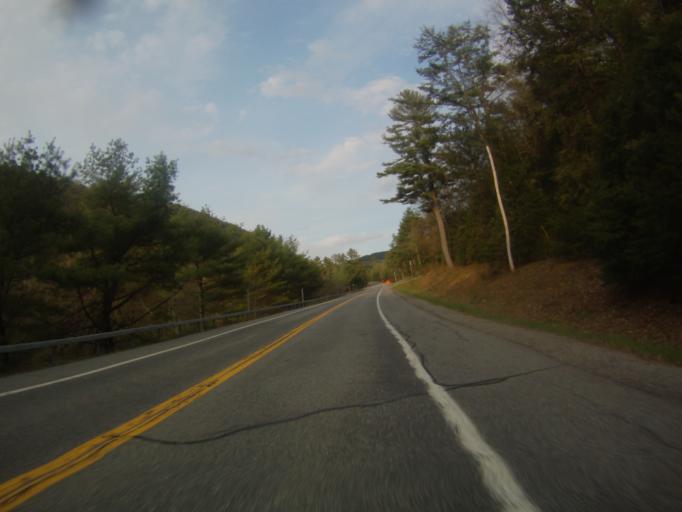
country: US
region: New York
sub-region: Essex County
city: Ticonderoga
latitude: 43.7416
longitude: -73.6530
